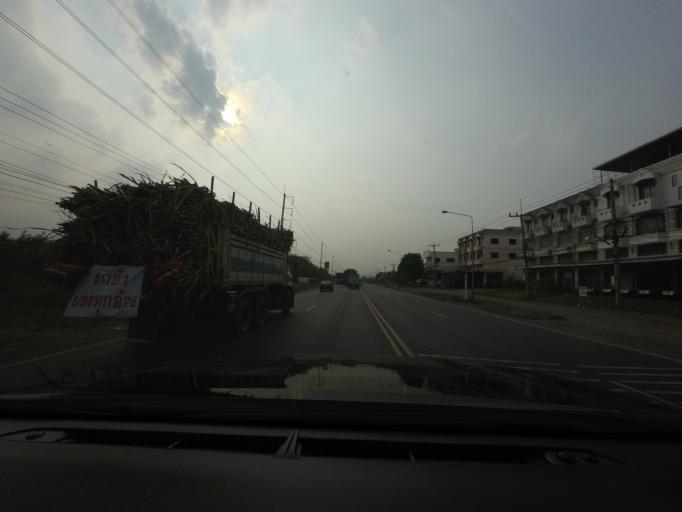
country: TH
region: Sara Buri
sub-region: Amphoe Wang Muang
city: Wang Muang
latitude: 14.8427
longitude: 101.1123
